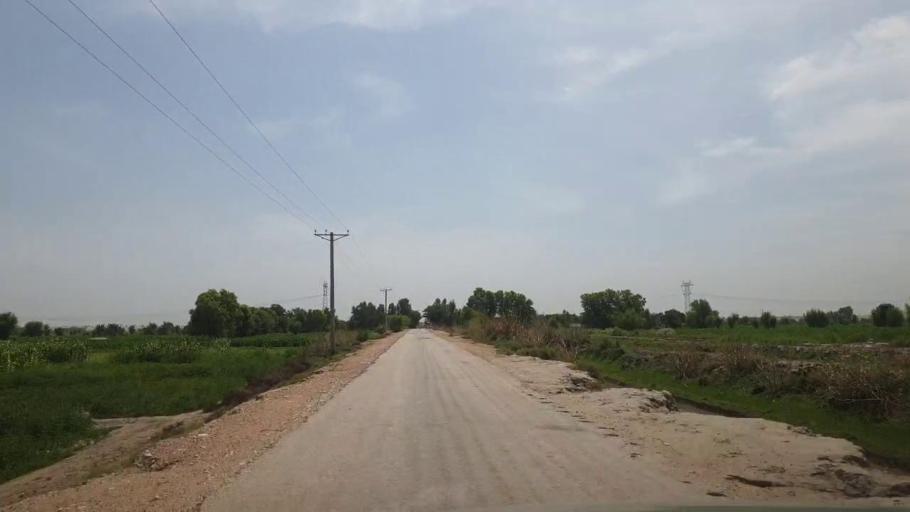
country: PK
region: Sindh
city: Kot Diji
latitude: 27.1083
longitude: 69.0338
